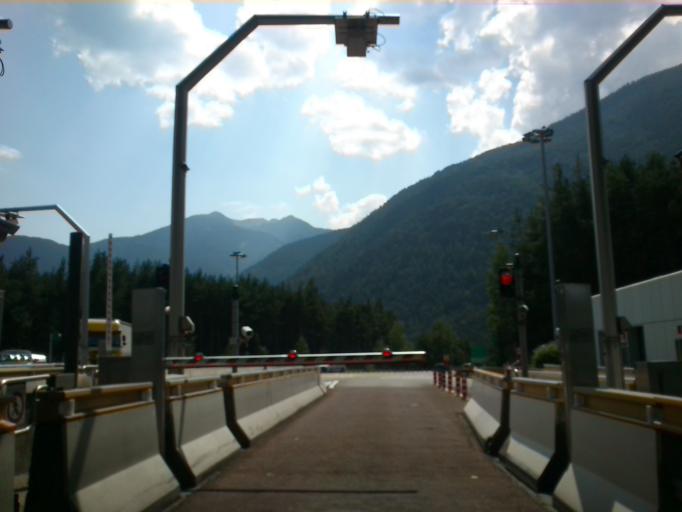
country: IT
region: Trentino-Alto Adige
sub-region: Bolzano
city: Naz-Sciaves - Natz-Schabs
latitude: 46.7641
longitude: 11.6417
